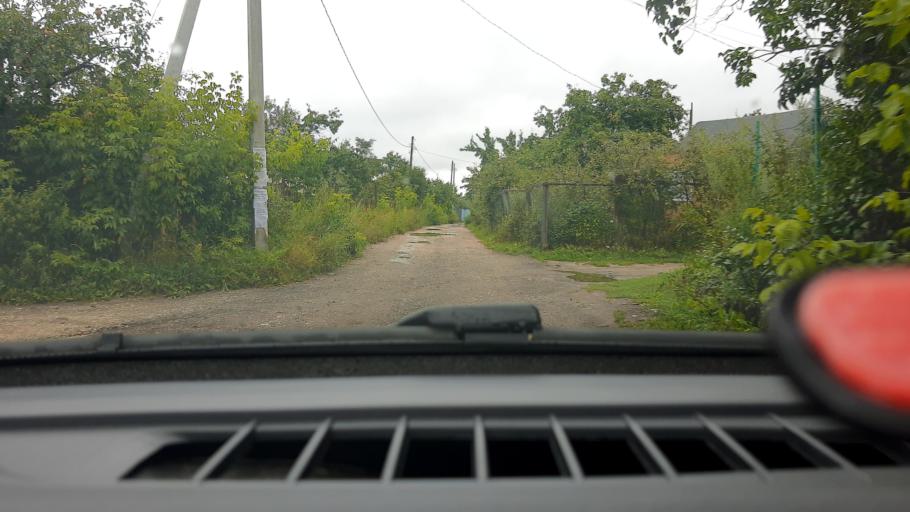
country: RU
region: Nizjnij Novgorod
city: Gorbatovka
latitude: 56.3193
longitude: 43.8372
